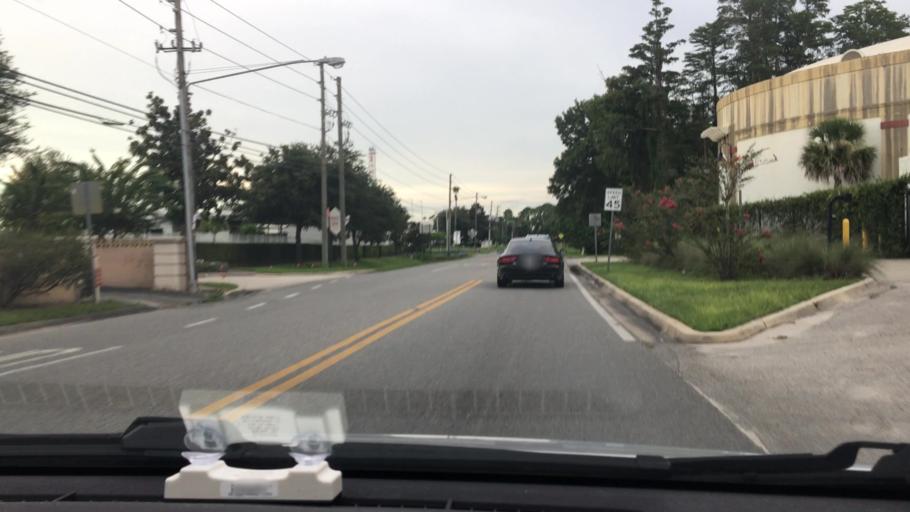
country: US
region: Florida
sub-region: Orange County
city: Eatonville
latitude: 28.6069
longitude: -81.3850
